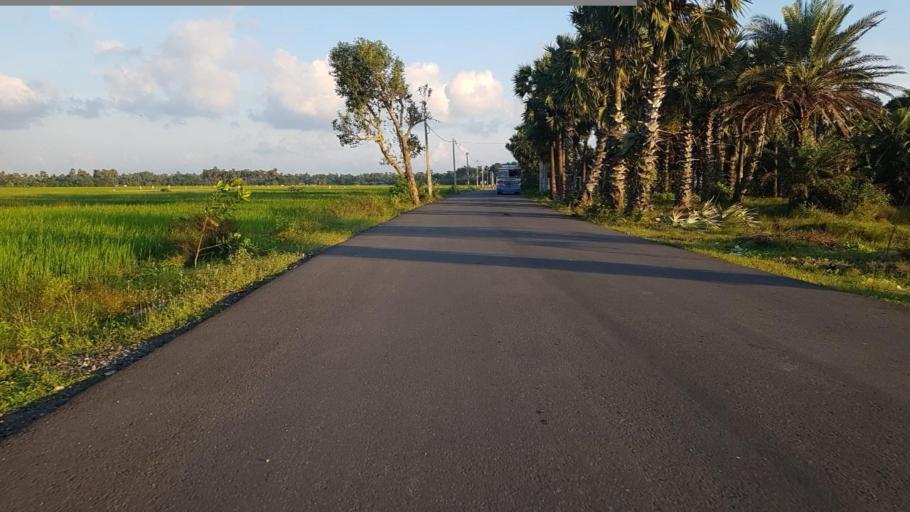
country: LK
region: Northern Province
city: Jaffna
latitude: 9.7270
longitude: 79.9733
